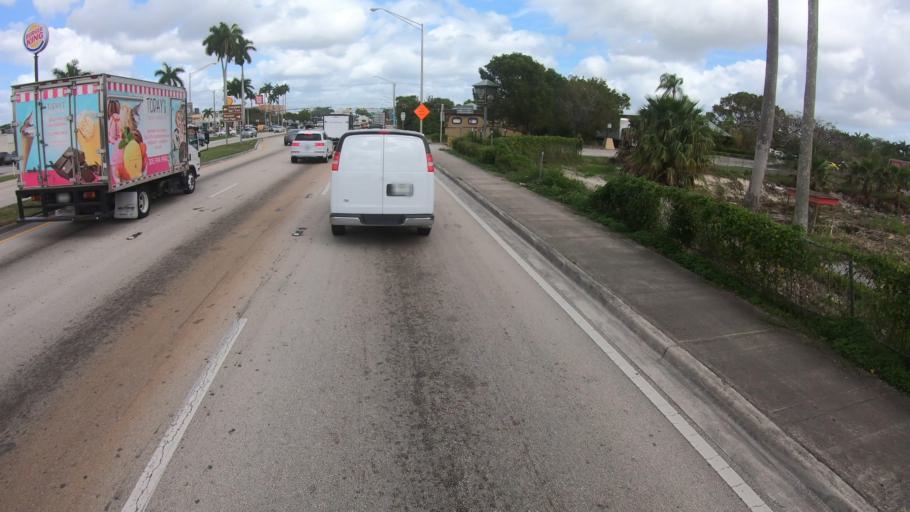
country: US
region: Florida
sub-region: Miami-Dade County
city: Florida City
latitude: 25.4462
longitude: -80.4744
